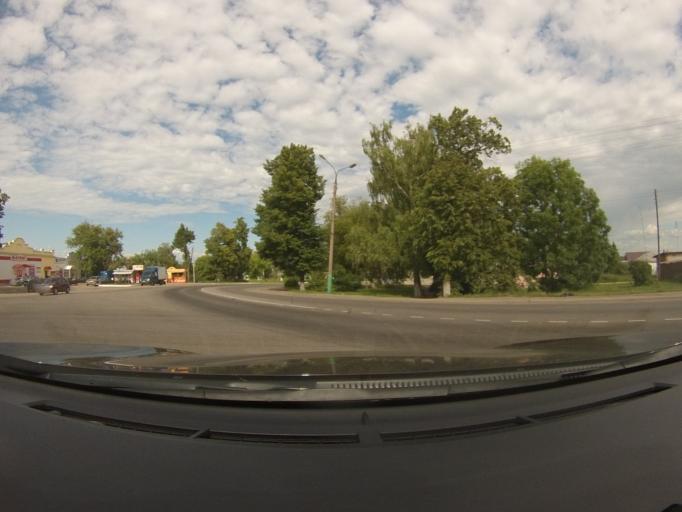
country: RU
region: Orjol
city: Mtsensk
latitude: 53.2853
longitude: 36.5562
